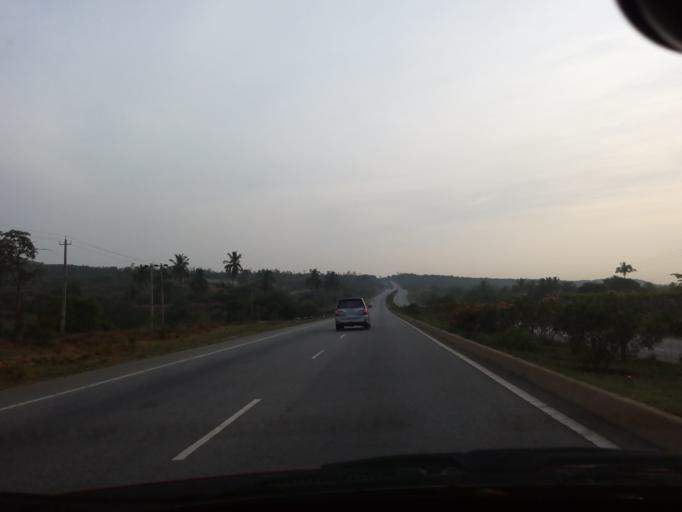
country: IN
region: Karnataka
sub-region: Chikkaballapur
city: Chik Ballapur
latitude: 13.5425
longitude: 77.7710
